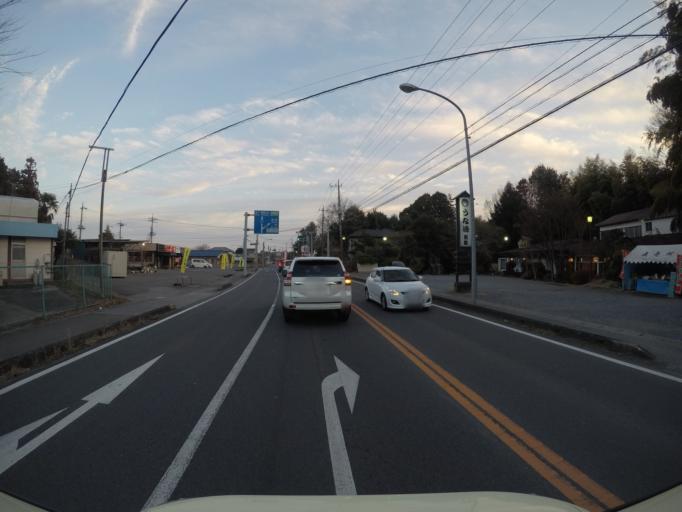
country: JP
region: Tochigi
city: Mooka
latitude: 36.4927
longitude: 139.9694
